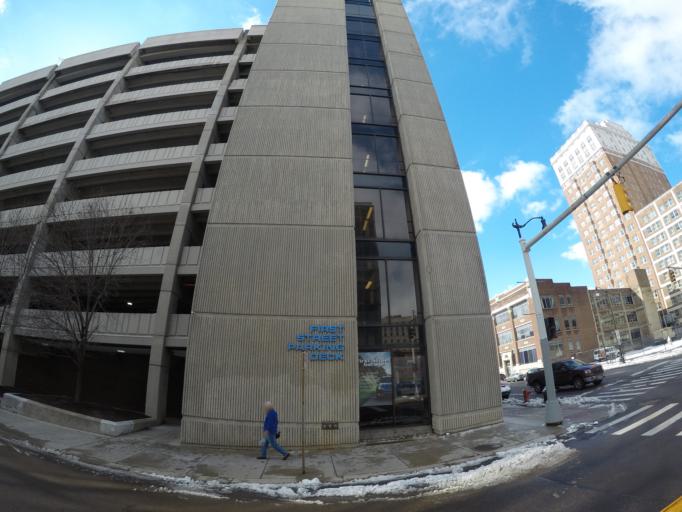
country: US
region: Michigan
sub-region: Wayne County
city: Detroit
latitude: 42.3283
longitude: -83.0516
